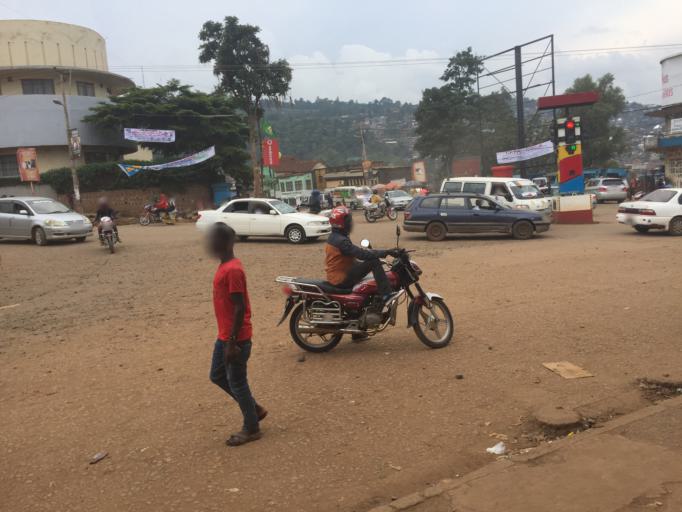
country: CD
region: South Kivu
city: Bukavu
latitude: -2.4966
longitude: 28.8551
